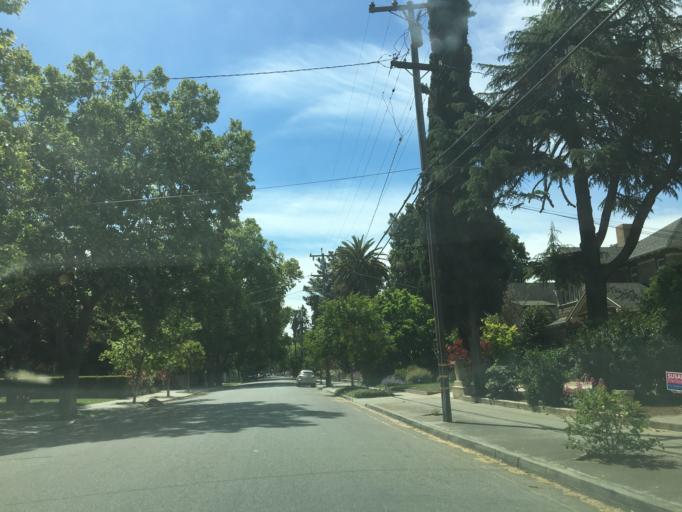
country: US
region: California
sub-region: Santa Clara County
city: Buena Vista
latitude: 37.3012
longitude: -121.9007
